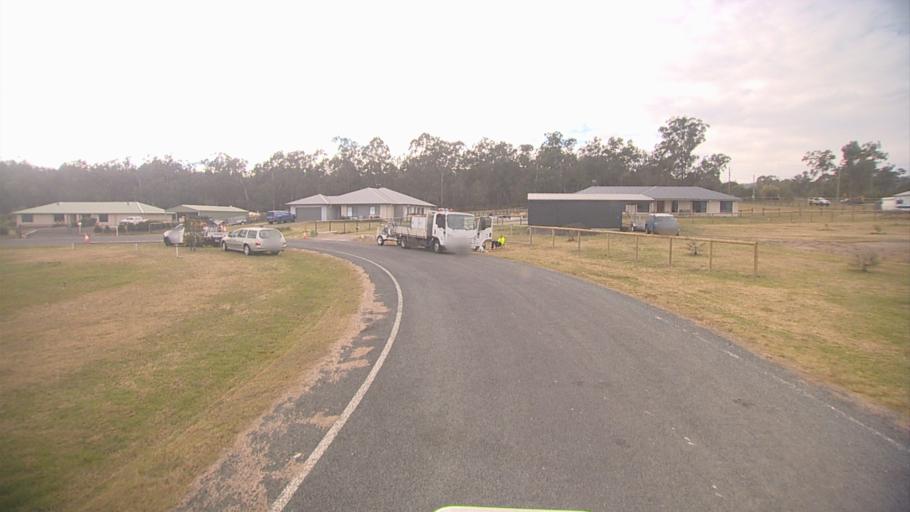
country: AU
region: Queensland
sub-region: Logan
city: Logan Reserve
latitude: -27.7510
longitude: 153.1398
